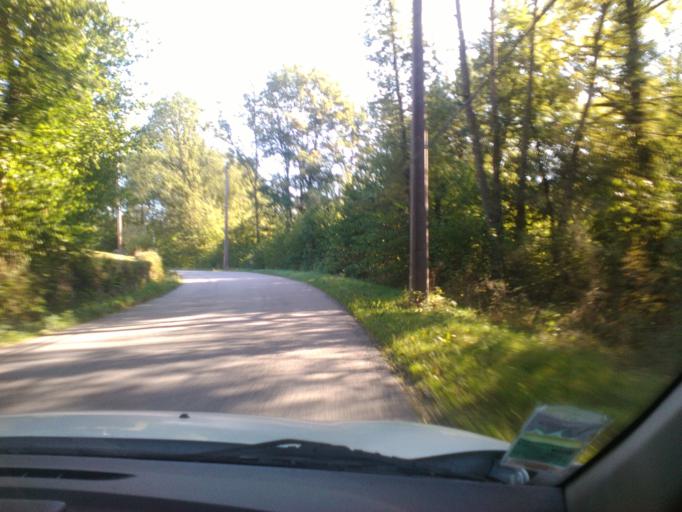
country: FR
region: Lorraine
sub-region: Departement des Vosges
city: Vagney
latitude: 48.0263
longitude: 6.7225
